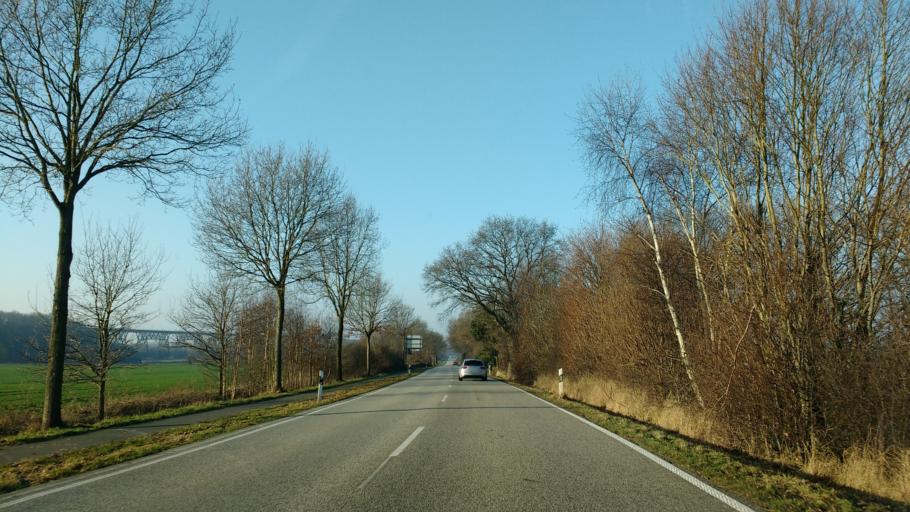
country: DE
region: Schleswig-Holstein
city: Gribbohm
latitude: 54.0174
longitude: 9.3266
